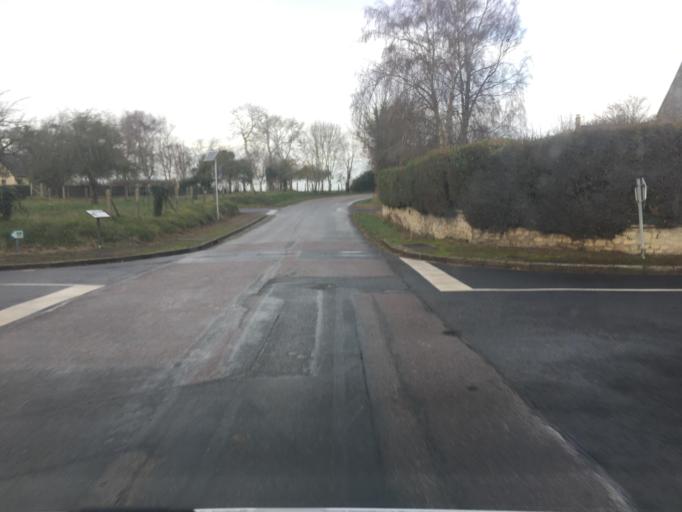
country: FR
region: Lower Normandy
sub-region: Departement du Calvados
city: Ver-sur-Mer
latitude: 49.3163
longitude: -0.5514
